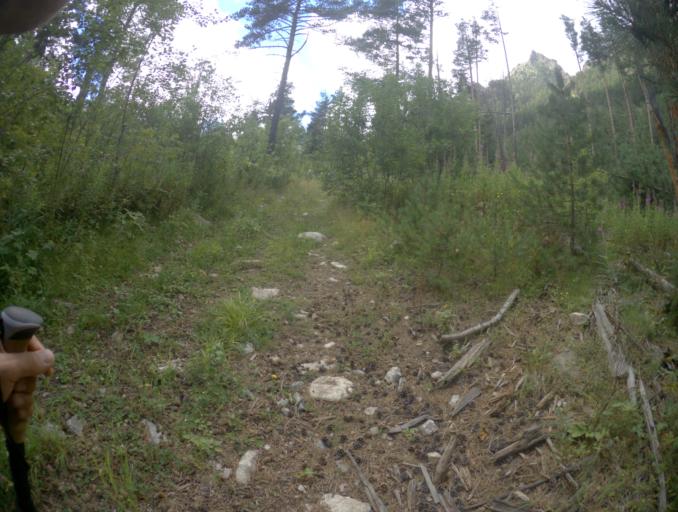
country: RU
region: Karachayevo-Cherkesiya
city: Uchkulan
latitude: 43.3538
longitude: 42.1637
